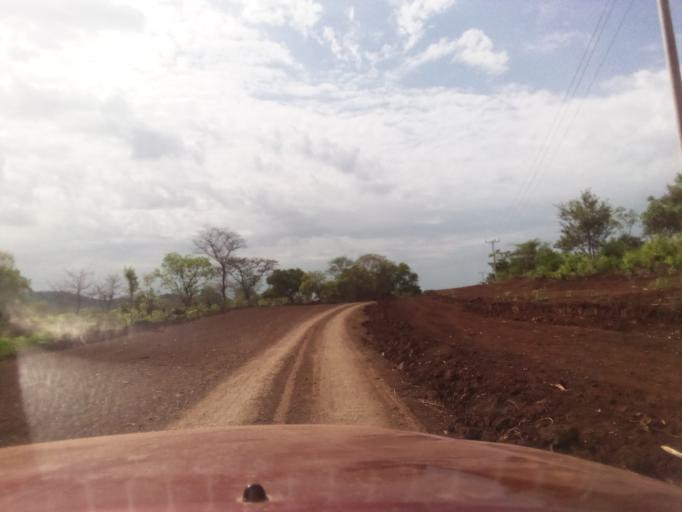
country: ET
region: Oromiya
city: Mendi
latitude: 10.0587
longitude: 35.2837
